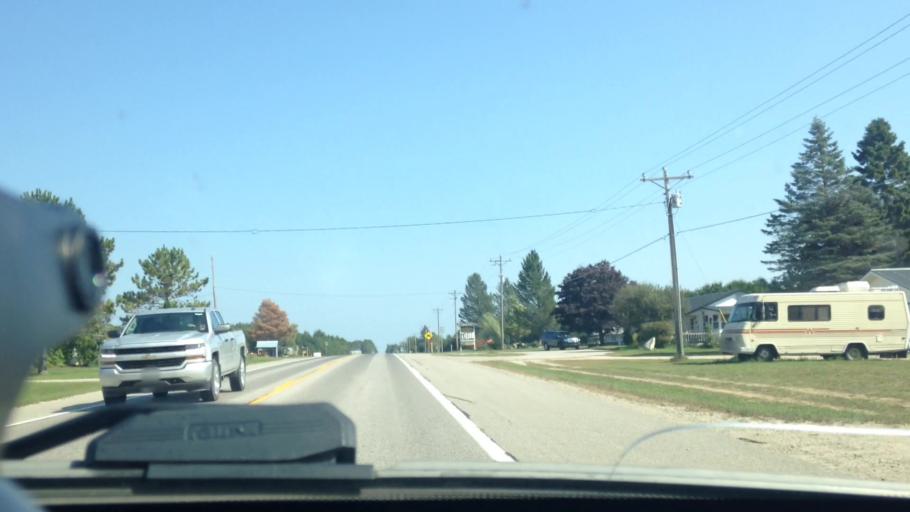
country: US
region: Michigan
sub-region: Luce County
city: Newberry
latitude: 46.3031
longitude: -85.5005
